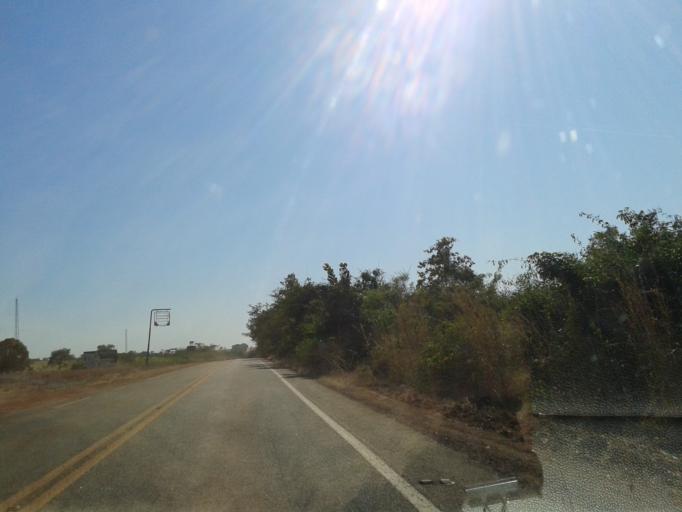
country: BR
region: Goias
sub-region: Mozarlandia
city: Mozarlandia
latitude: -14.4115
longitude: -50.4471
